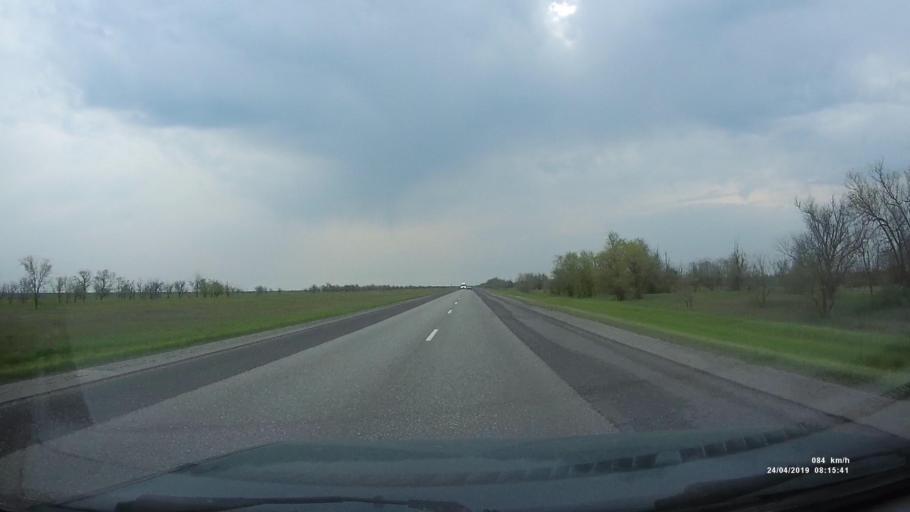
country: RU
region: Kalmykiya
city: Priyutnoye
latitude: 46.0998
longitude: 43.5986
